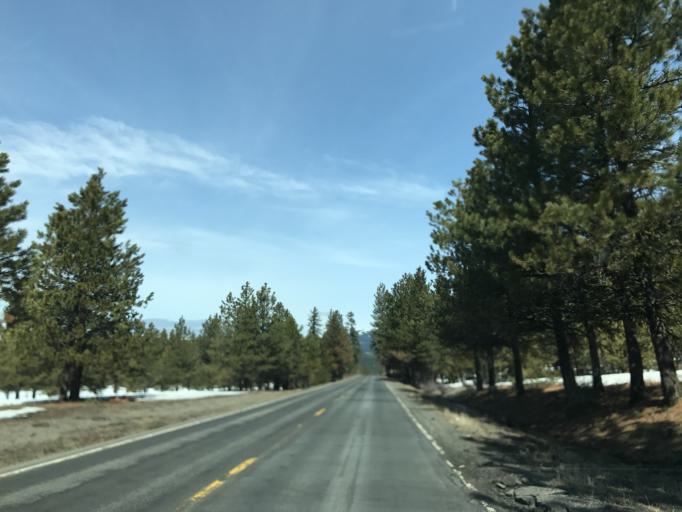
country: US
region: Idaho
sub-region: Valley County
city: McCall
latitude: 44.9385
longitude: -116.1662
